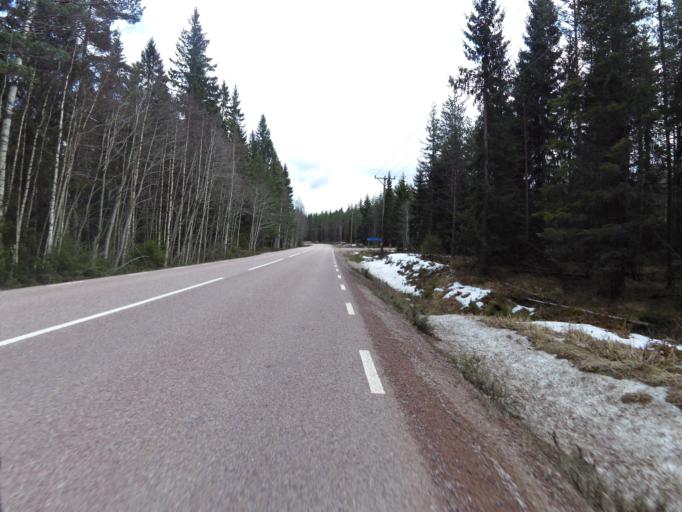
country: SE
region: Dalarna
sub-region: Avesta Kommun
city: Horndal
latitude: 60.2873
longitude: 16.3129
